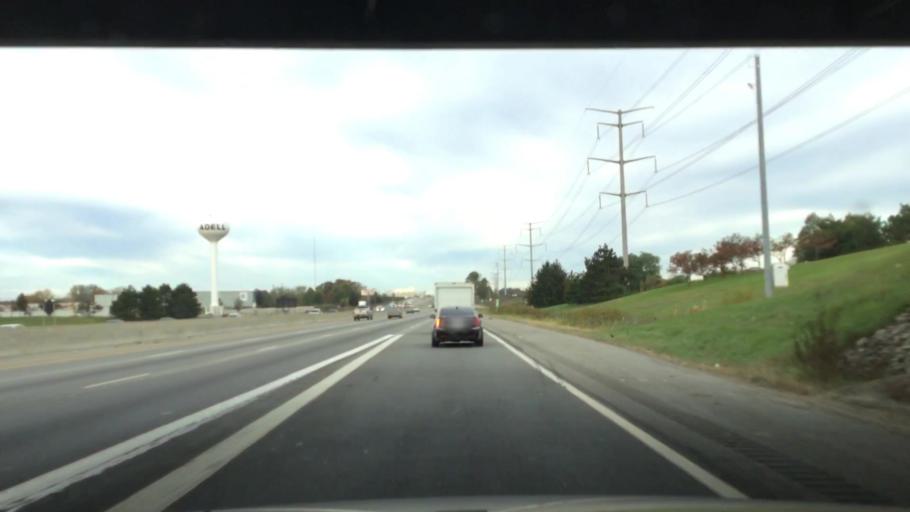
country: US
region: Michigan
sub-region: Oakland County
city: Novi
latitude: 42.4872
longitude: -83.4762
